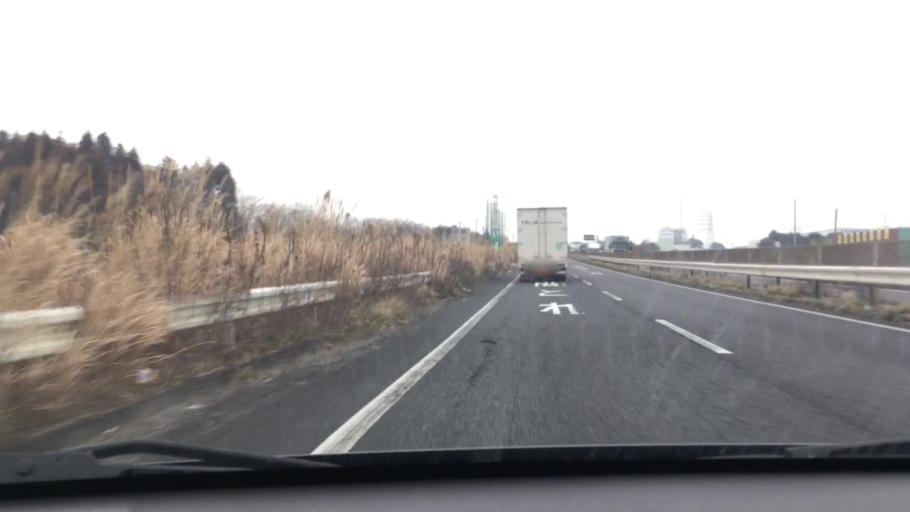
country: JP
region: Mie
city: Ueno-ebisumachi
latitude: 34.7156
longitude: 136.0803
